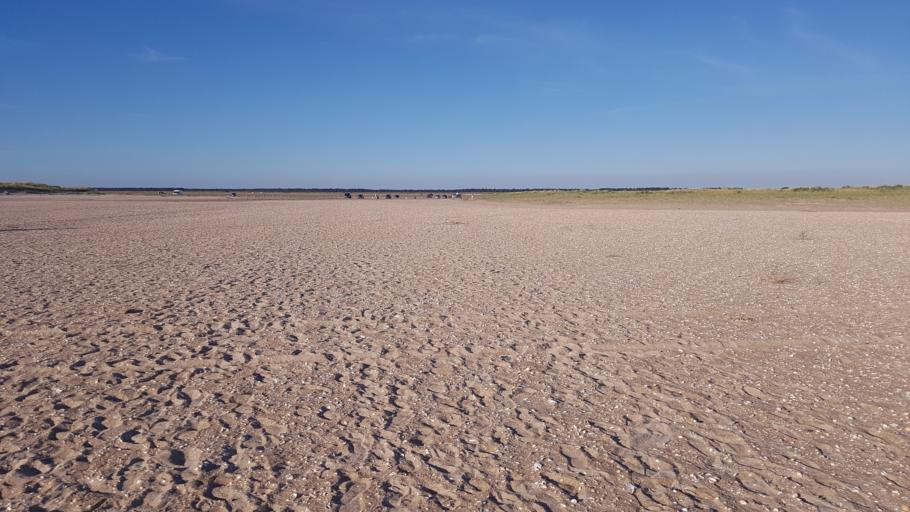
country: DE
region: Schleswig-Holstein
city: List
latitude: 55.0732
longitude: 8.4917
